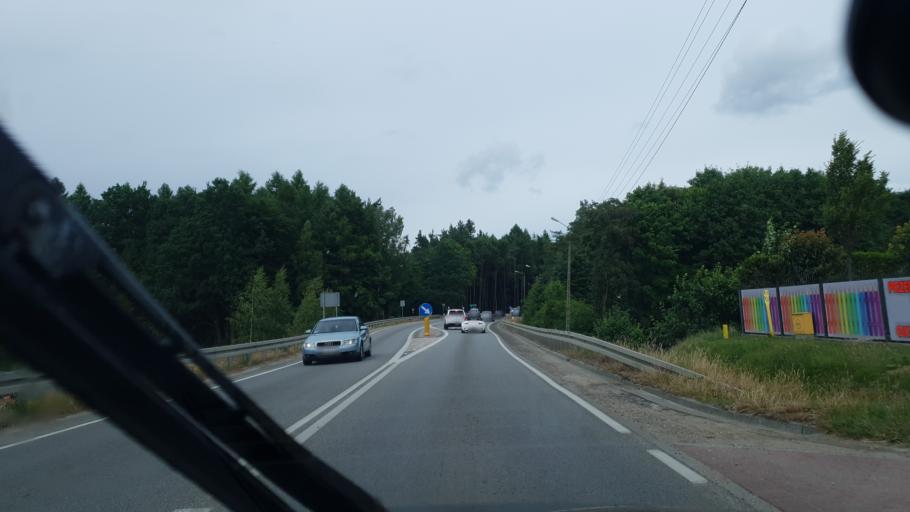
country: PL
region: Pomeranian Voivodeship
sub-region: Powiat kartuski
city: Chwaszczyno
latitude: 54.4302
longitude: 18.3911
